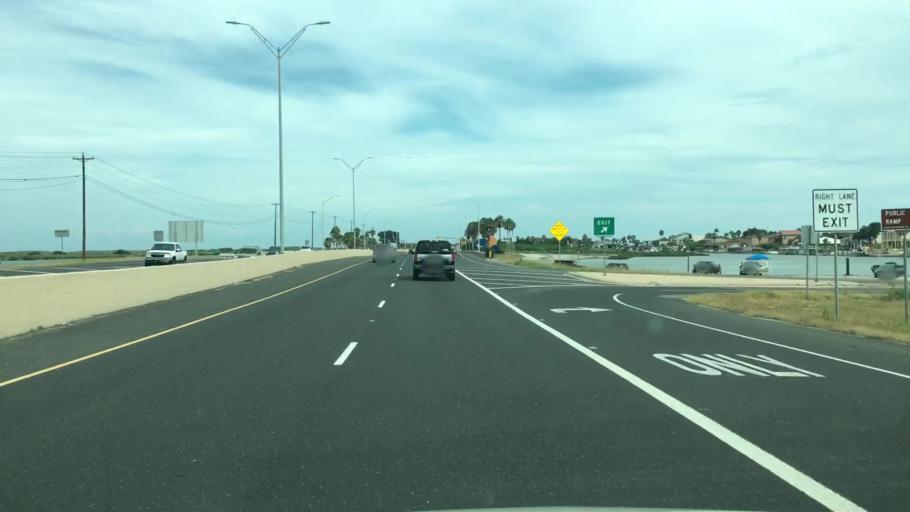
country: US
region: Texas
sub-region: Nueces County
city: Corpus Christi
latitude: 27.6323
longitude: -97.2342
